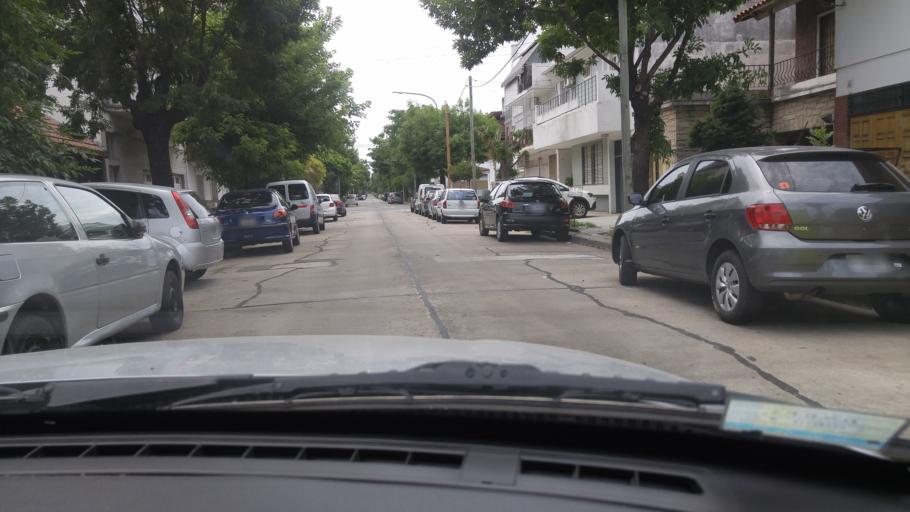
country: AR
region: Buenos Aires F.D.
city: Villa Santa Rita
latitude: -34.6337
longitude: -58.5106
